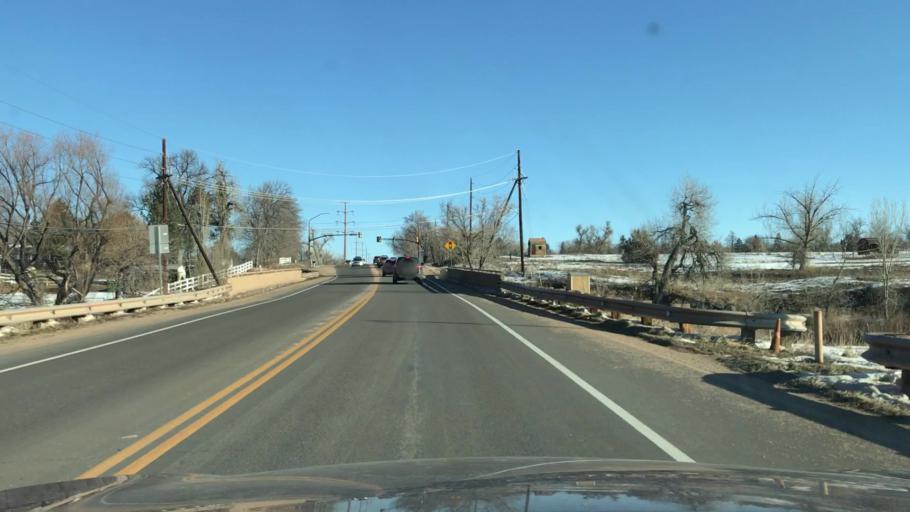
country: US
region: Colorado
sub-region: Boulder County
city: Gunbarrel
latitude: 40.0512
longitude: -105.1783
